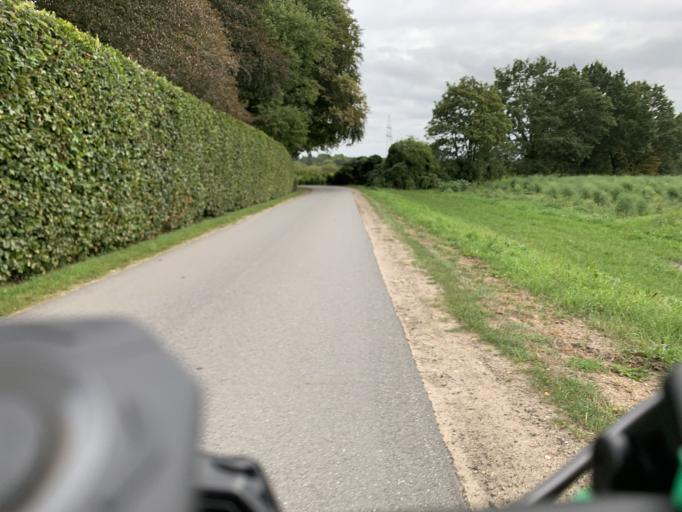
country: DE
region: Lower Saxony
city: Westerstede
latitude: 53.2409
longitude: 7.9229
